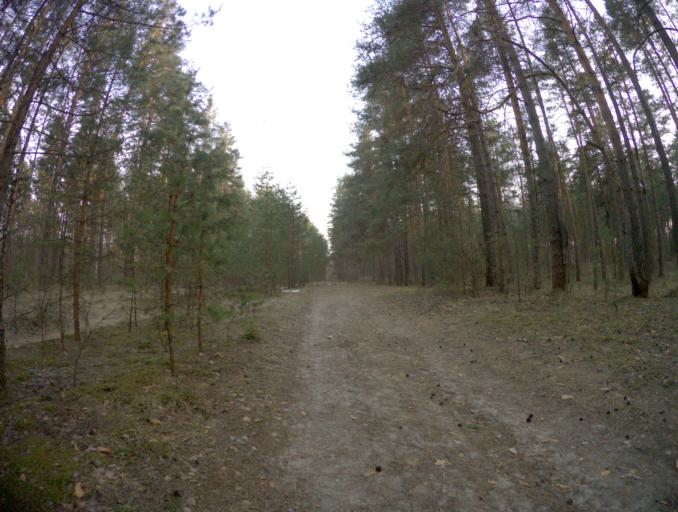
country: RU
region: Vladimir
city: Kommunar
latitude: 56.0670
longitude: 40.4490
